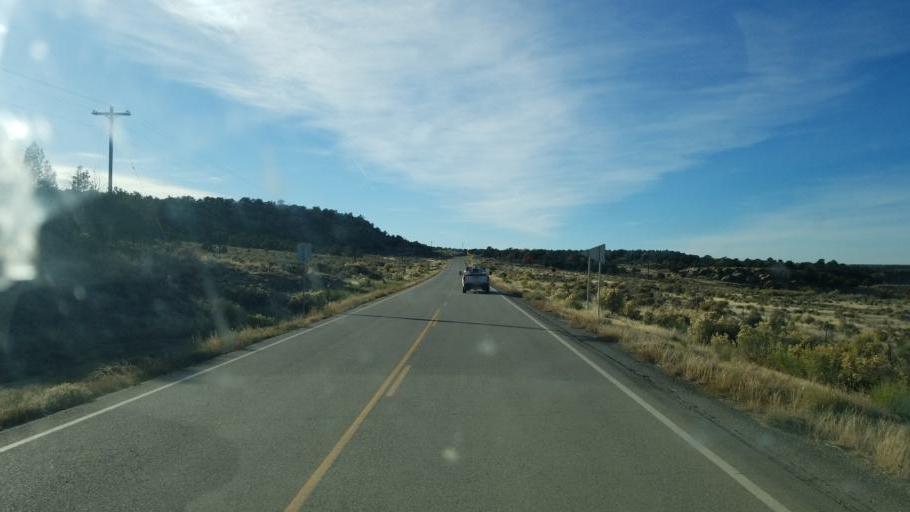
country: US
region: New Mexico
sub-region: San Juan County
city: Bloomfield
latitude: 36.7472
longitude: -107.5863
